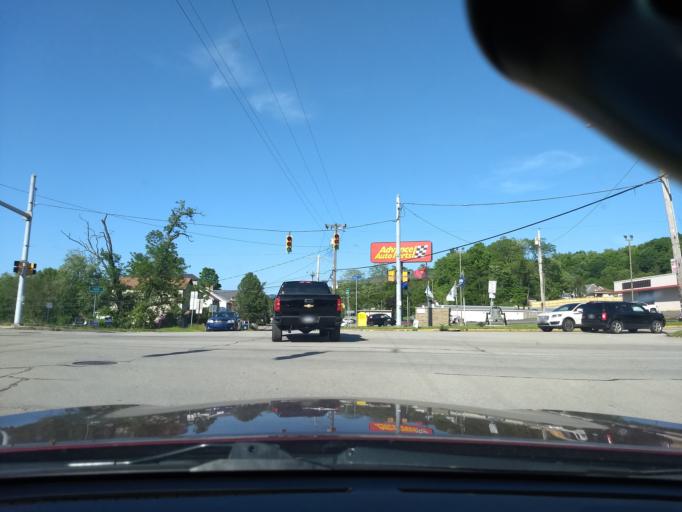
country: US
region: Pennsylvania
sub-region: Allegheny County
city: Versailles
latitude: 40.3105
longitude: -79.8268
